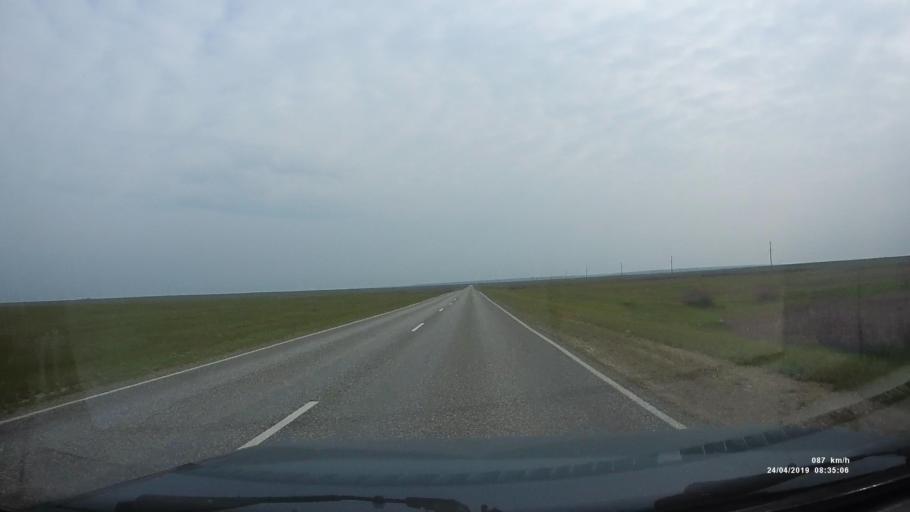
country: RU
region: Kalmykiya
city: Arshan'
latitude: 46.1952
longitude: 43.9142
